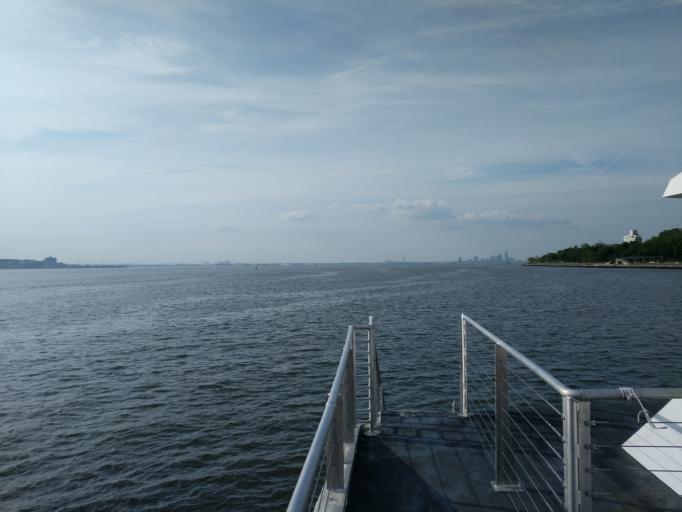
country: US
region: New York
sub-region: Kings County
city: Bensonhurst
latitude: 40.6158
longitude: -74.0433
